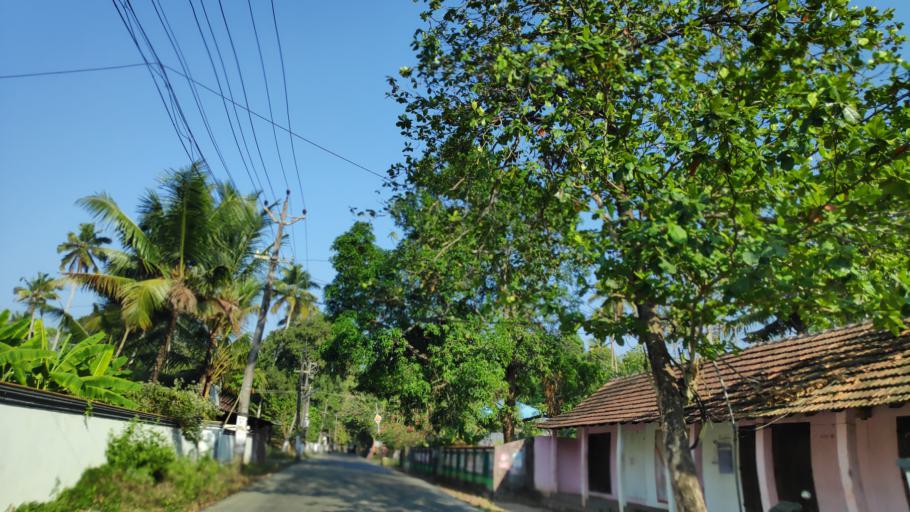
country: IN
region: Kerala
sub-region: Alappuzha
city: Alleppey
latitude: 9.5702
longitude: 76.3145
